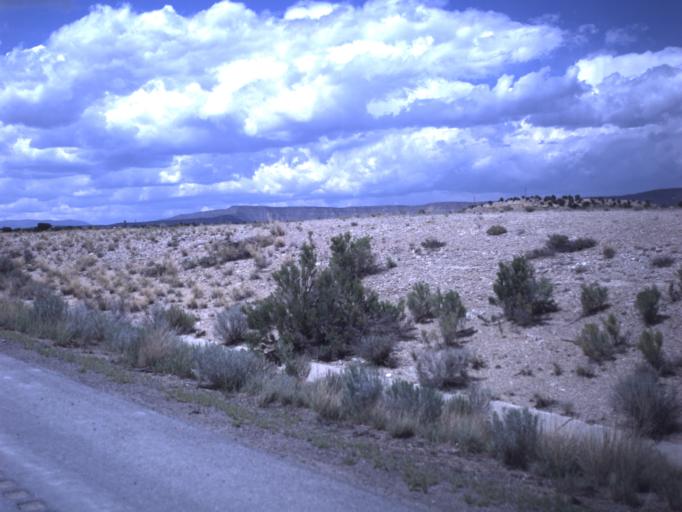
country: US
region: Utah
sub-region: Duchesne County
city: Duchesne
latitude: 40.1748
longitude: -110.5036
